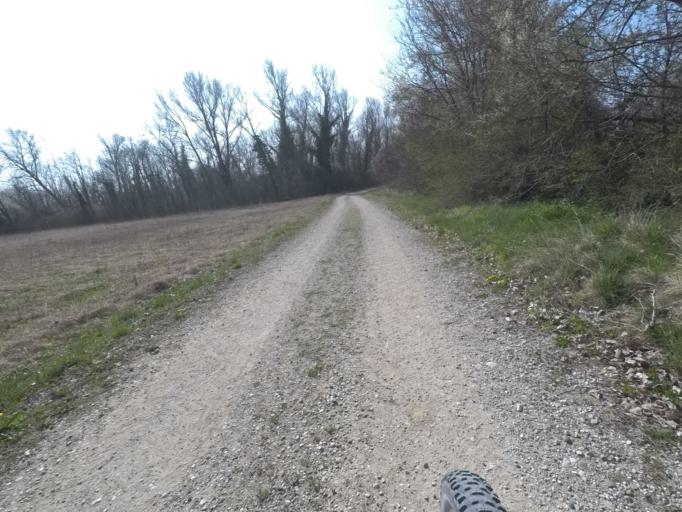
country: IT
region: Friuli Venezia Giulia
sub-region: Provincia di Udine
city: Remanzacco
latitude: 46.0644
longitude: 13.3288
